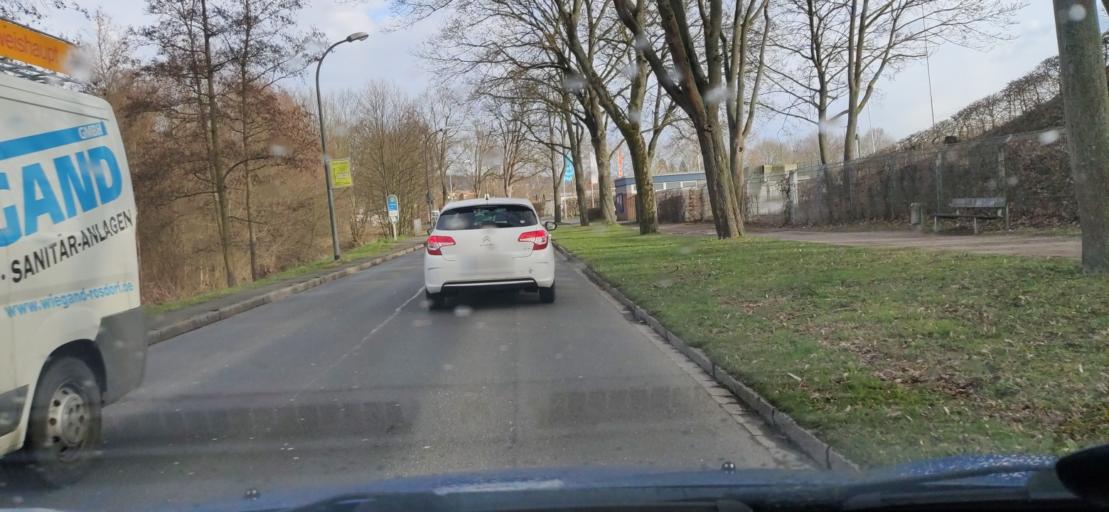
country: DE
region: Lower Saxony
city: Goettingen
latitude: 51.5205
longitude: 9.9266
